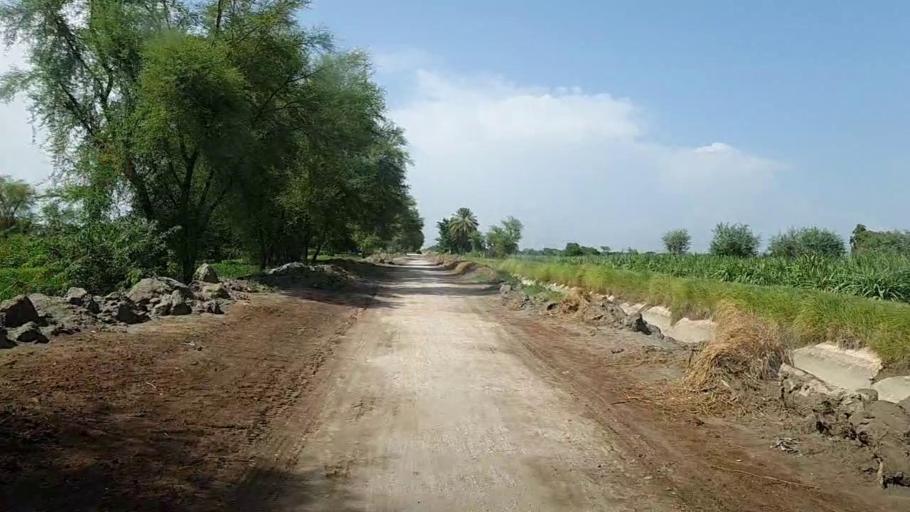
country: PK
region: Sindh
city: Bhiria
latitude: 26.8936
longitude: 68.2370
